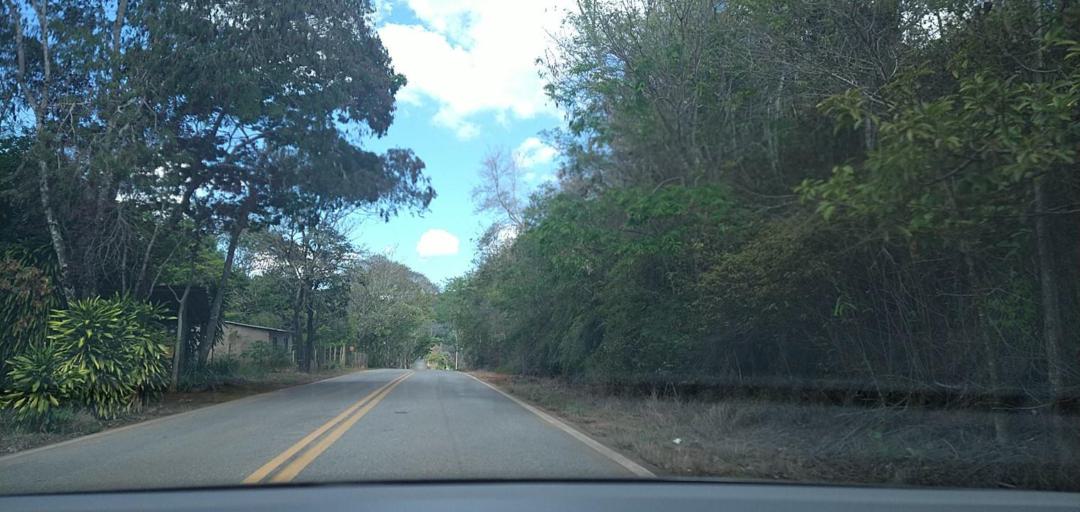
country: BR
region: Minas Gerais
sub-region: Rio Piracicaba
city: Rio Piracicaba
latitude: -20.0028
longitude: -43.1021
